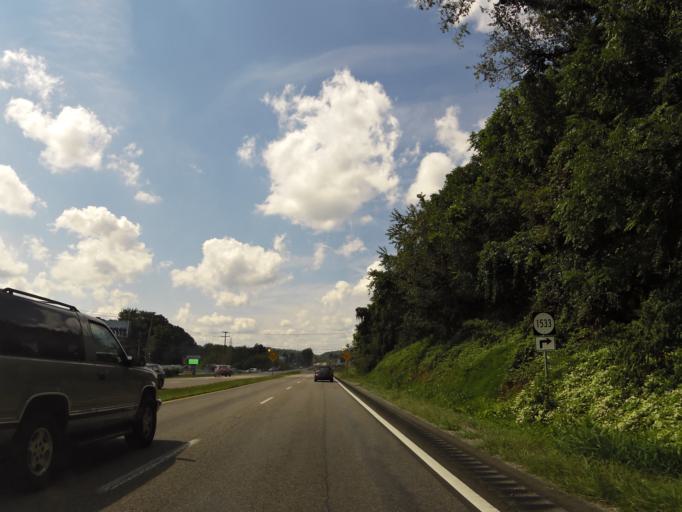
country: US
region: Virginia
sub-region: Washington County
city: Abingdon
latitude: 36.7177
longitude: -82.0067
